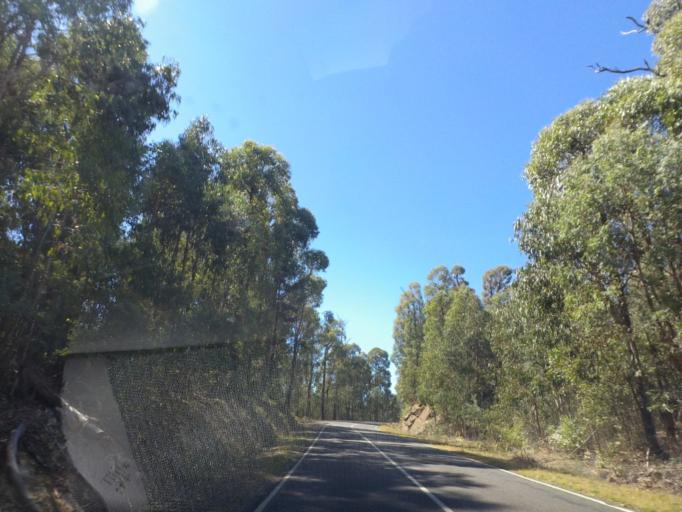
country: AU
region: Victoria
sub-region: Yarra Ranges
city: Millgrove
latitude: -37.5172
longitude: 145.7790
